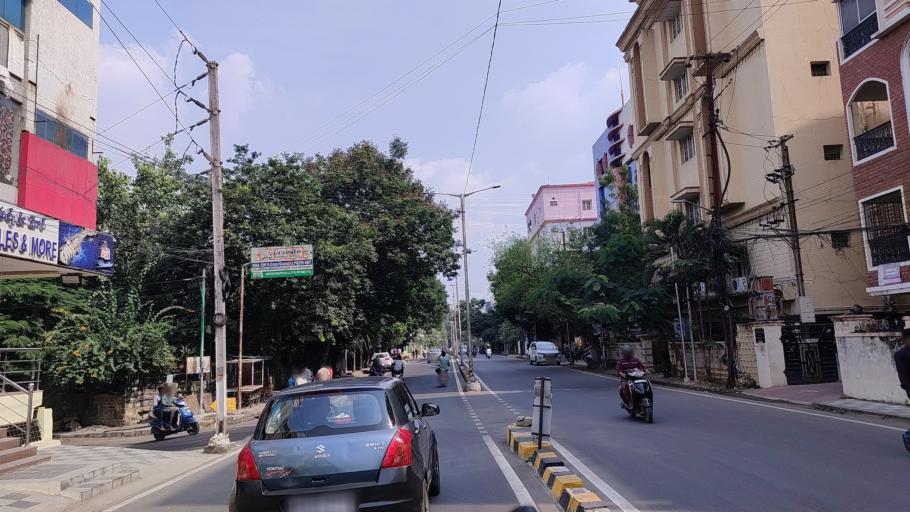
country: IN
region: Telangana
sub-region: Hyderabad
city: Hyderabad
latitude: 17.4301
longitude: 78.4417
